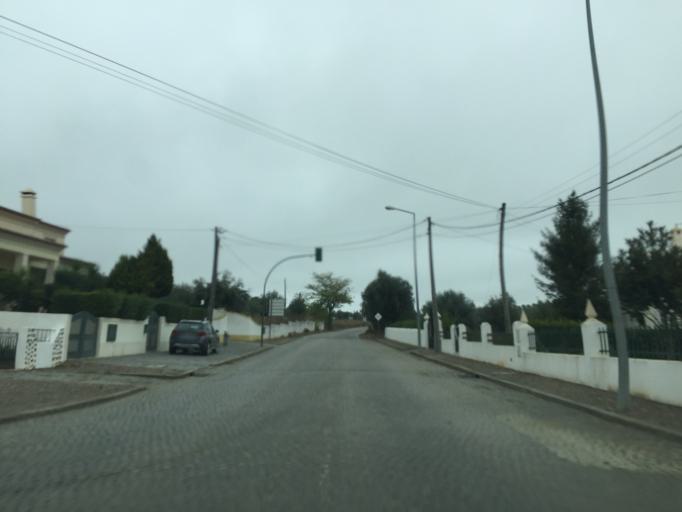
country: PT
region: Portalegre
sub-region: Alter do Chao
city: Alter do Chao
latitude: 39.2052
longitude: -7.6572
